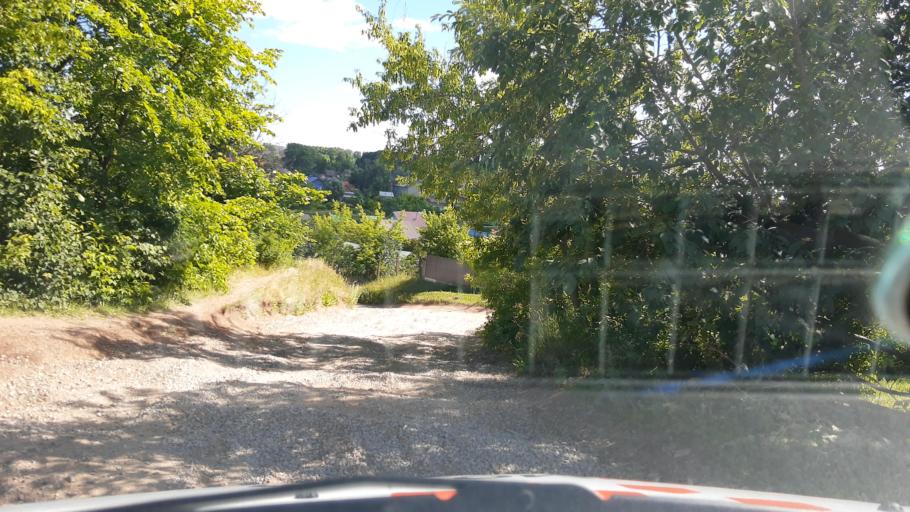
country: RU
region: Bashkortostan
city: Iglino
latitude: 54.8400
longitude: 56.4205
